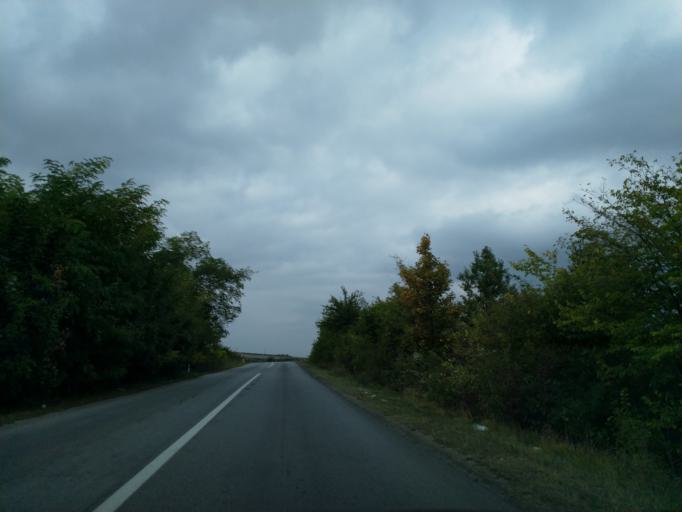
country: RS
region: Central Serbia
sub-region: Sumadijski Okrug
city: Topola
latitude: 44.1547
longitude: 20.7402
